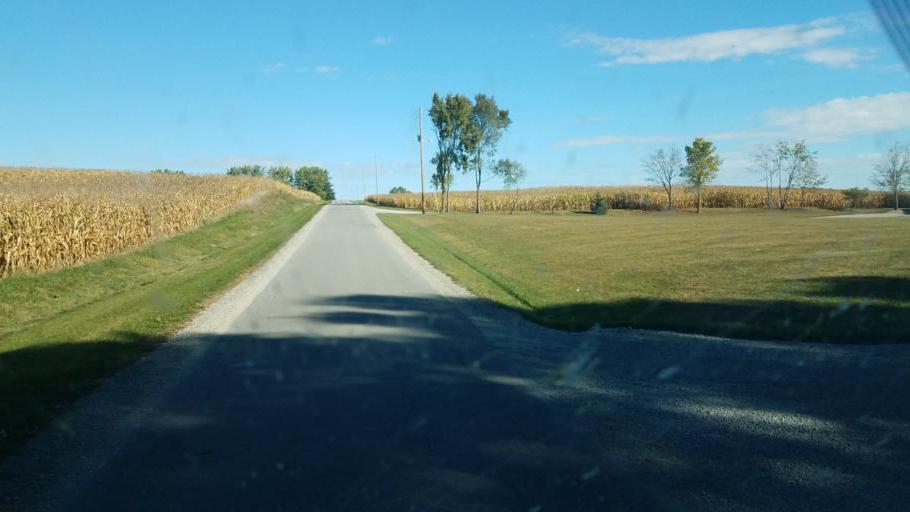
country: US
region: Ohio
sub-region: Wyandot County
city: Upper Sandusky
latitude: 40.7710
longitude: -83.2075
